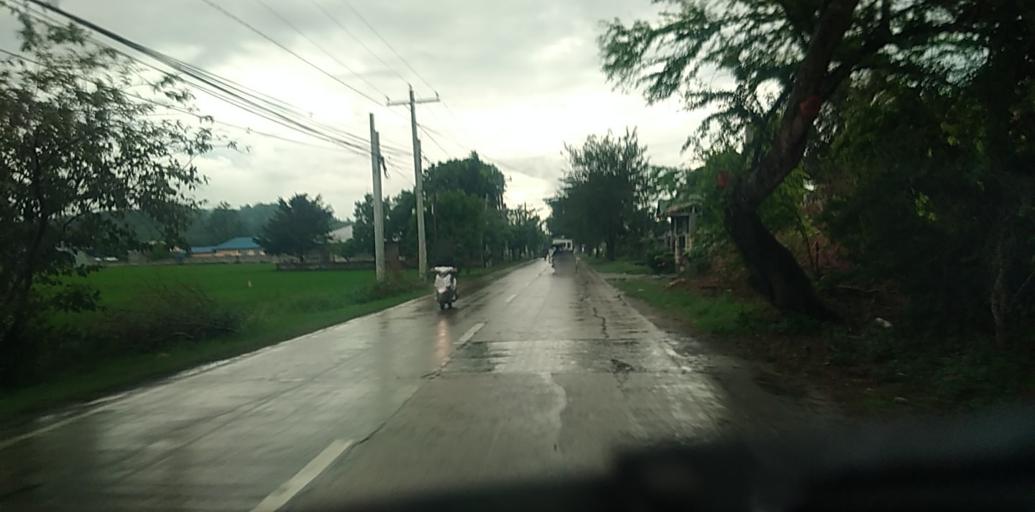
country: PH
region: Central Luzon
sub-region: Province of Pampanga
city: Arayat
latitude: 15.1533
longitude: 120.7315
